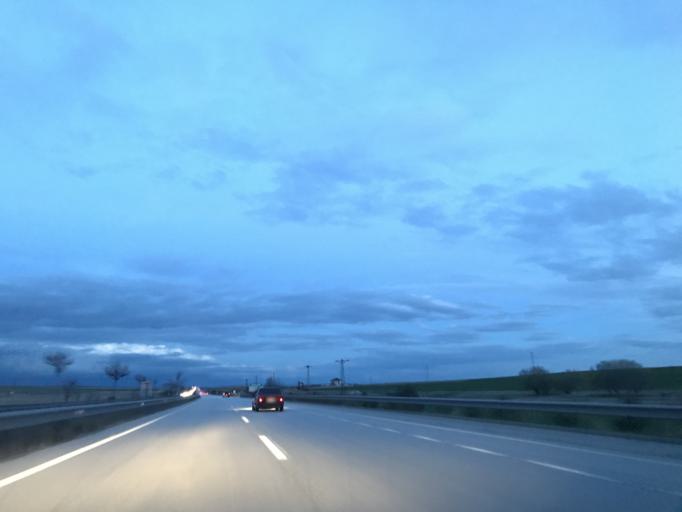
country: TR
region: Konya
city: Kulu
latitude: 39.1763
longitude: 33.1423
